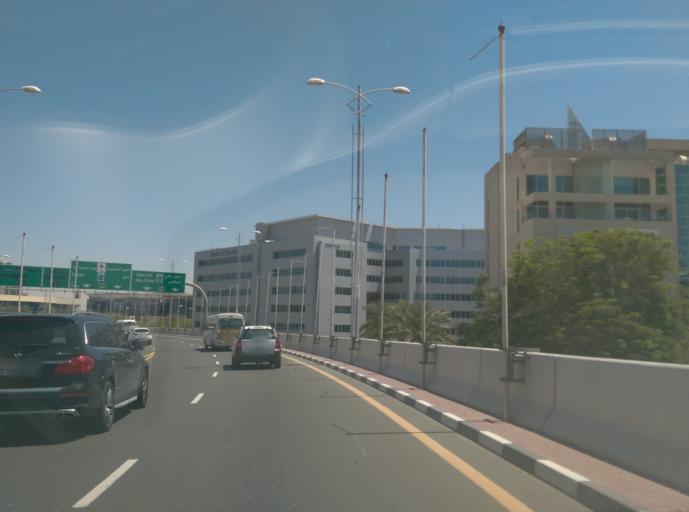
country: AE
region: Dubai
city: Dubai
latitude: 25.0975
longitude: 55.1580
